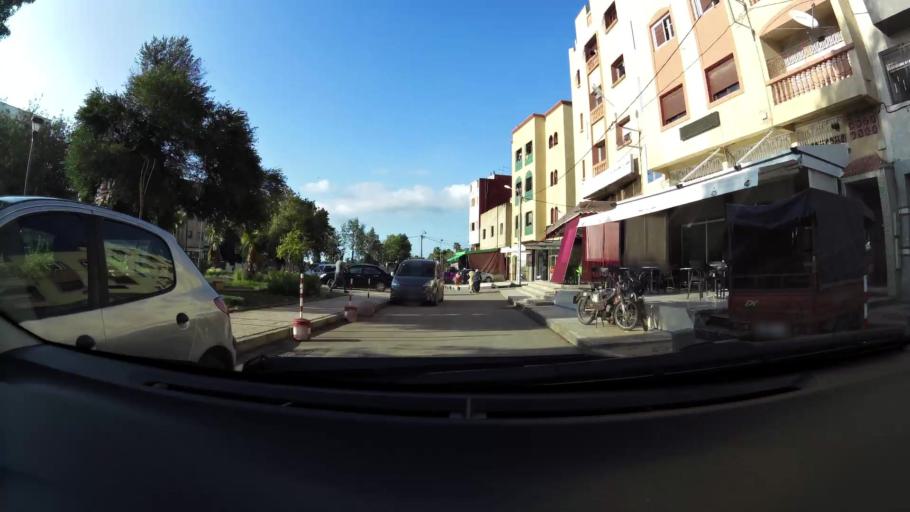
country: MA
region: Chaouia-Ouardigha
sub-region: Settat Province
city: Settat
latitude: 33.0047
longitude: -7.6210
